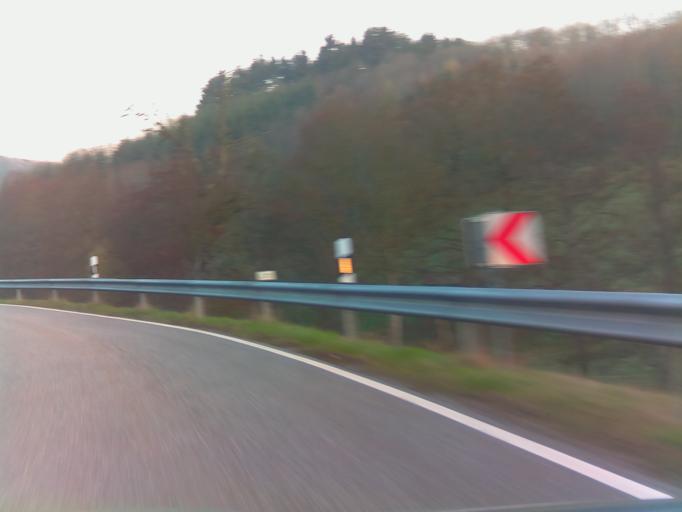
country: DE
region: Rheinland-Pfalz
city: Kirrweiler
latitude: 49.6274
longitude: 7.5039
